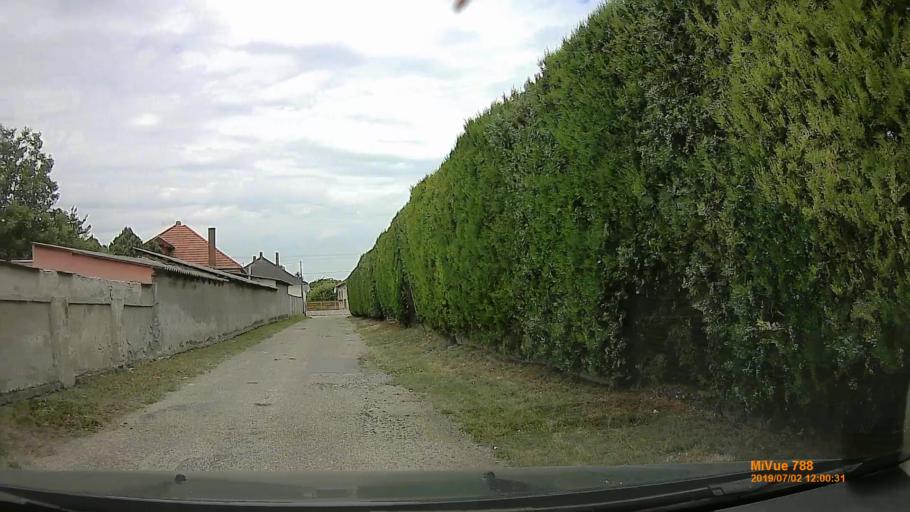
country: HU
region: Gyor-Moson-Sopron
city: Janossomorja
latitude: 47.8494
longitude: 17.1732
